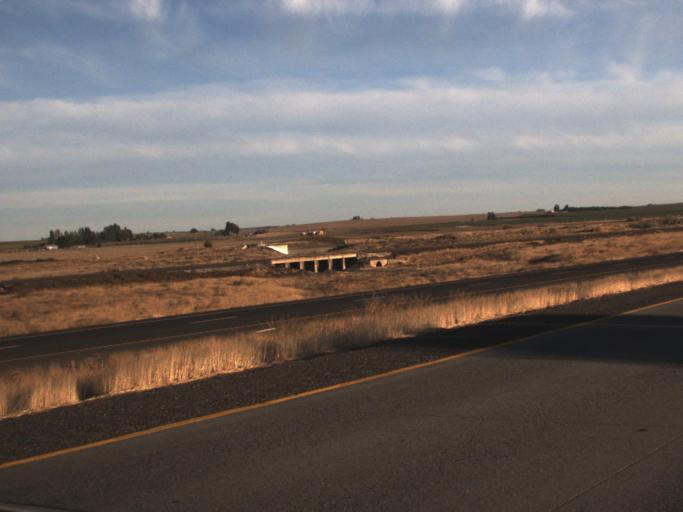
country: US
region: Washington
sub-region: Franklin County
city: Pasco
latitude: 46.3611
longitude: -119.0849
